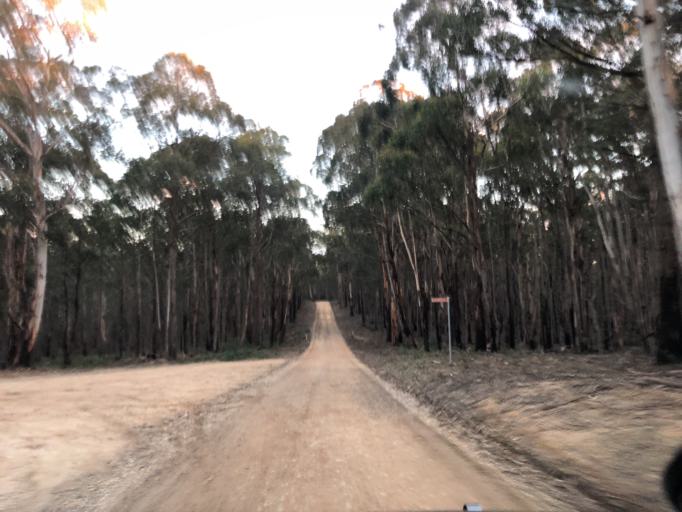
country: AU
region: Victoria
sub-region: Moorabool
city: Bacchus Marsh
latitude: -37.4816
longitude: 144.4363
